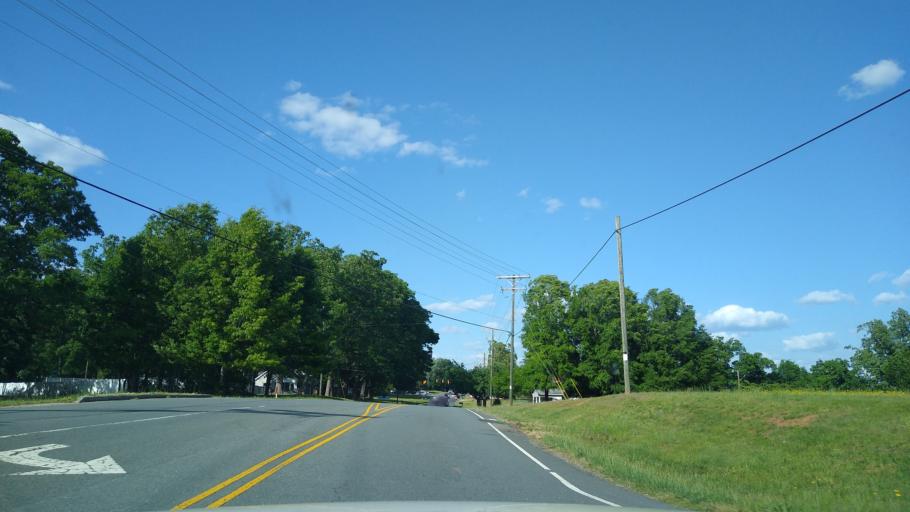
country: US
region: North Carolina
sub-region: Forsyth County
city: Kernersville
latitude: 36.0984
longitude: -80.0847
